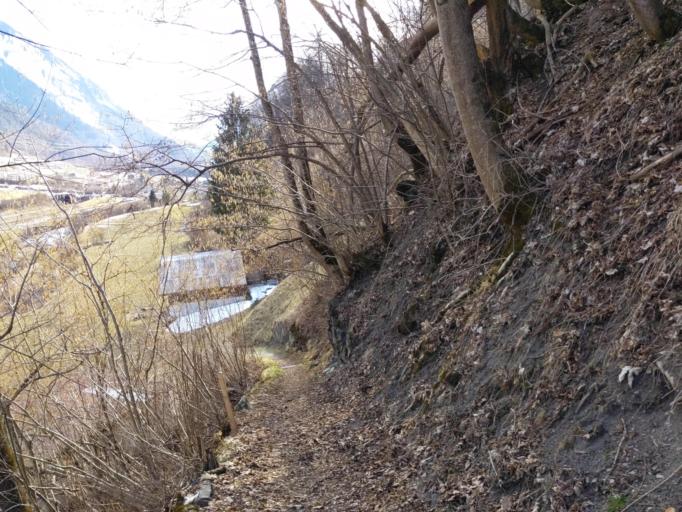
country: CH
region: Glarus
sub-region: Glarus
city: Luchsingen
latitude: 46.9438
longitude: 9.0207
